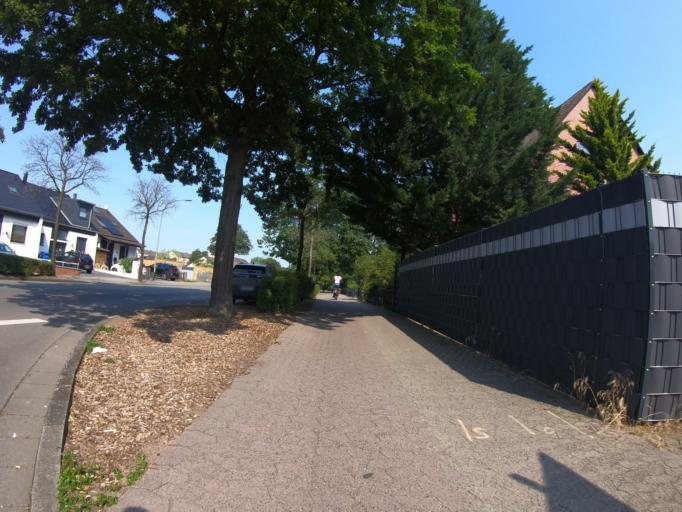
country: DE
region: Lower Saxony
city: Gifhorn
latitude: 52.4733
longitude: 10.5602
